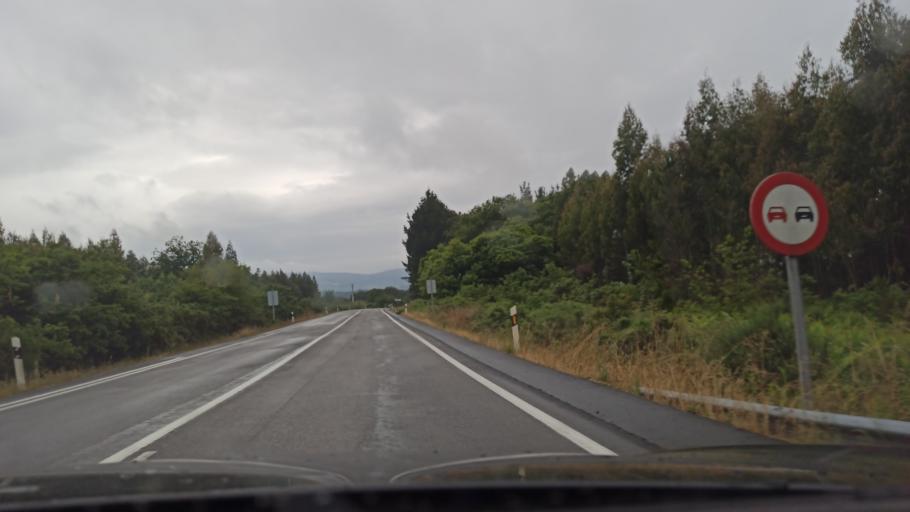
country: ES
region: Galicia
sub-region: Provincia de Lugo
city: Monterroso
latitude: 42.8034
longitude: -7.7849
